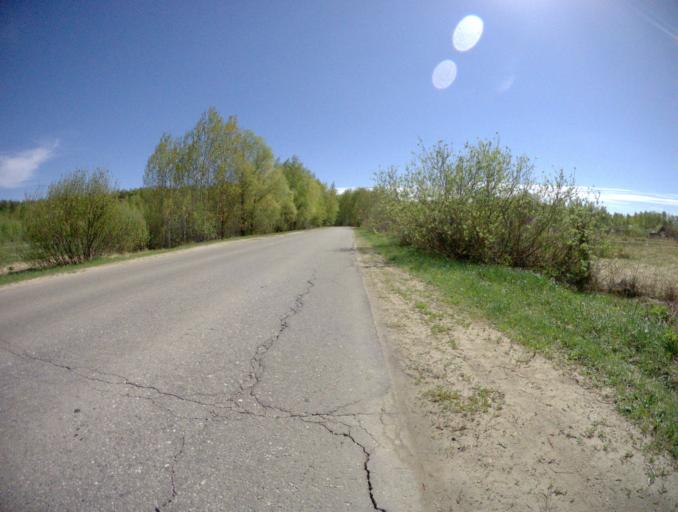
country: RU
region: Vladimir
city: Orgtrud
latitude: 56.1994
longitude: 40.5892
